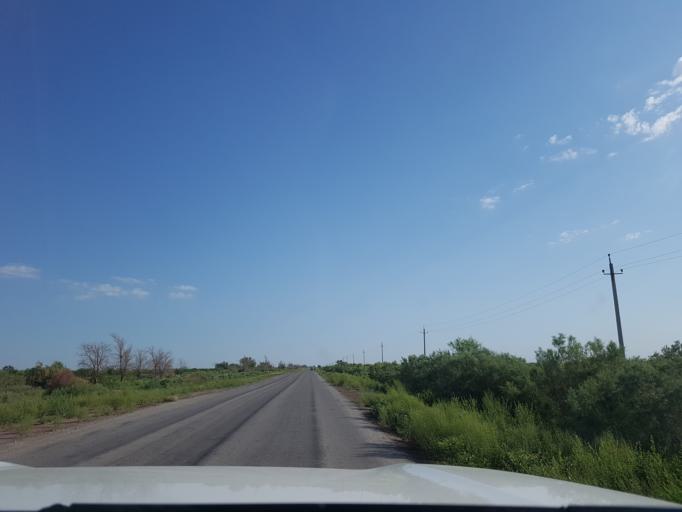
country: TM
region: Dasoguz
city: Koeneuergench
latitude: 41.8853
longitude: 58.7067
